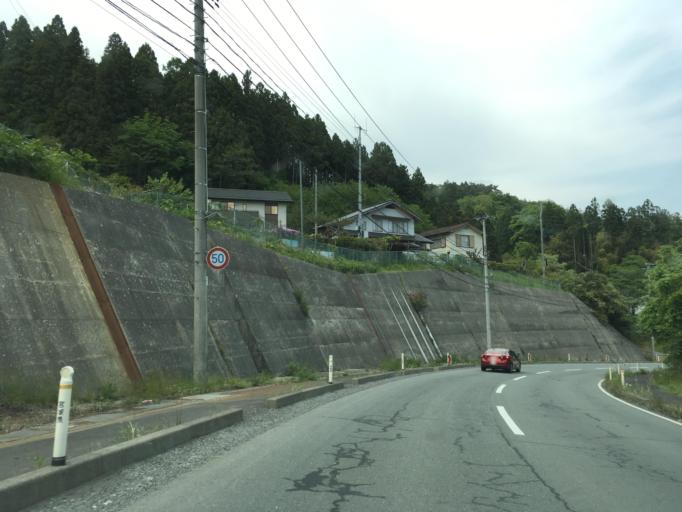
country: JP
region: Iwate
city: Ofunato
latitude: 38.8792
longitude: 141.5384
